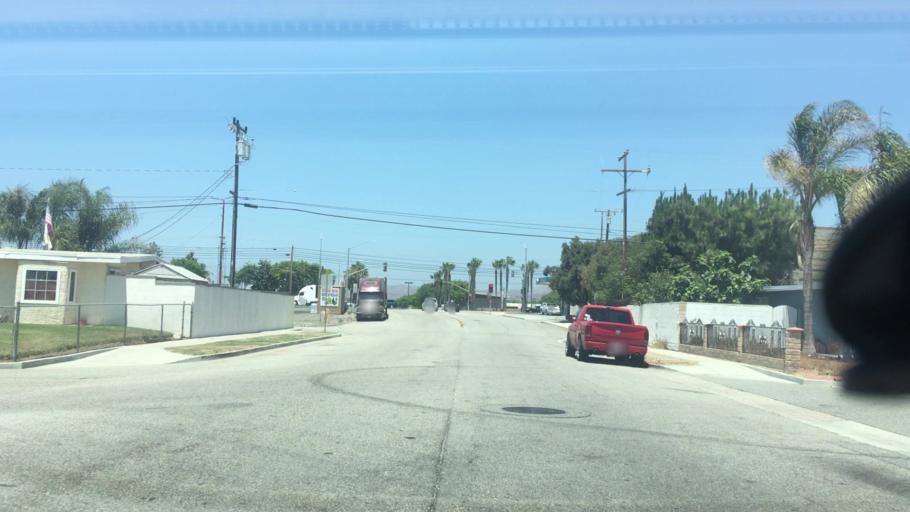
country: US
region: California
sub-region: Ventura County
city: El Rio
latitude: 34.2432
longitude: -119.1627
